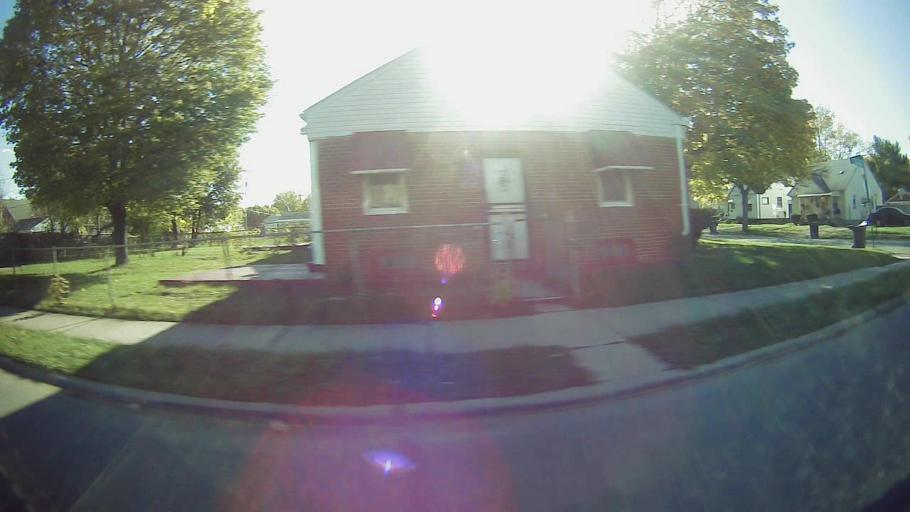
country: US
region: Michigan
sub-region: Wayne County
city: Dearborn Heights
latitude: 42.3532
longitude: -83.2235
